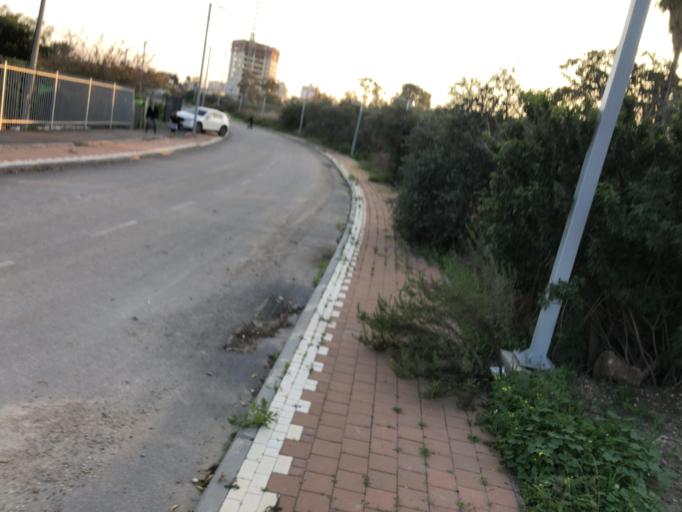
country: IL
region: Northern District
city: `Akko
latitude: 32.9324
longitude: 35.0827
